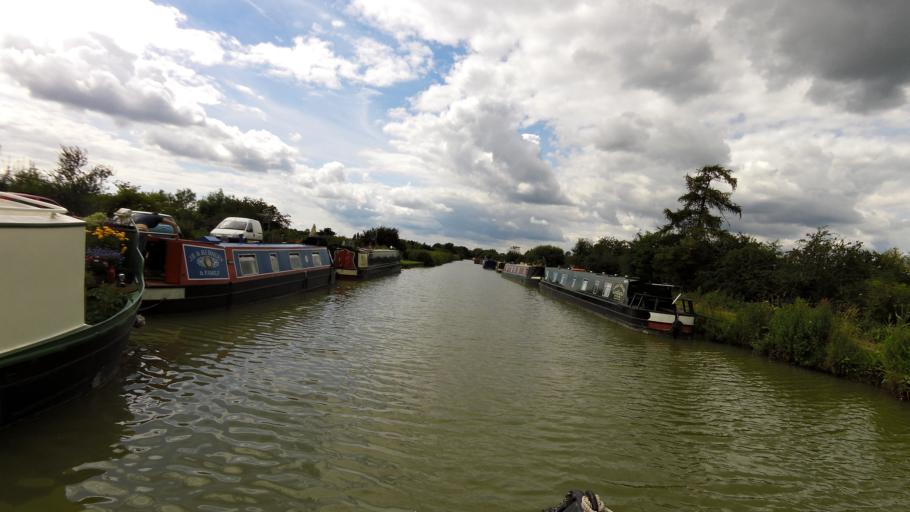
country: GB
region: England
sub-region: Wiltshire
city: Seend
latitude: 51.3545
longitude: -2.0557
